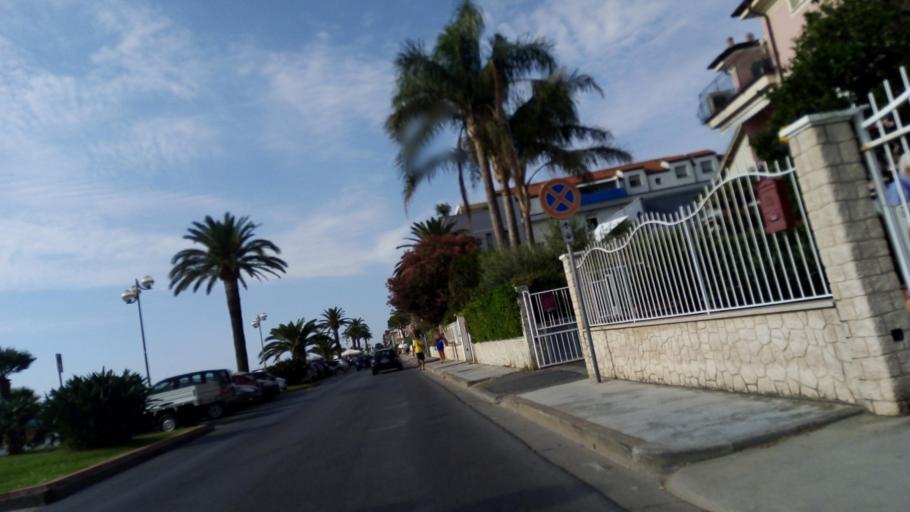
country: IT
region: Liguria
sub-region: Provincia di Savona
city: Ceriale
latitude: 44.0924
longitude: 8.2309
